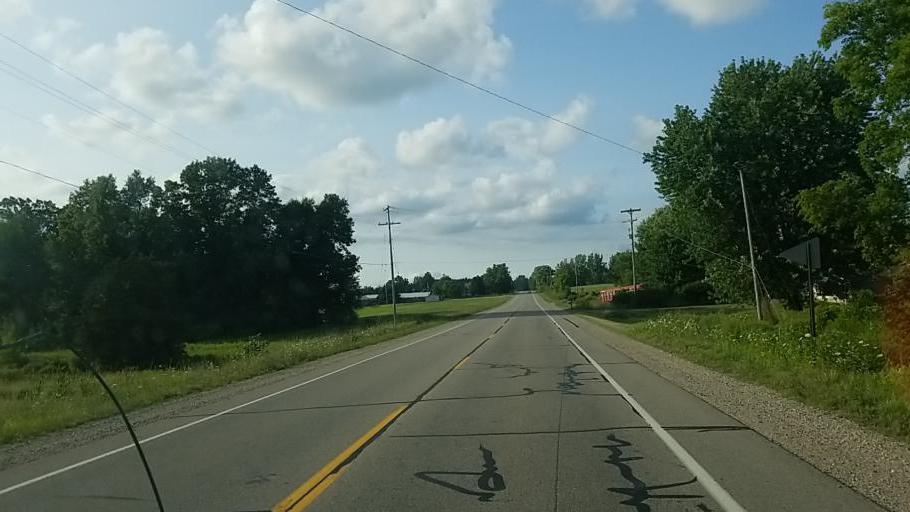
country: US
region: Michigan
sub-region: Kent County
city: Lowell
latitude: 43.0229
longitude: -85.3519
